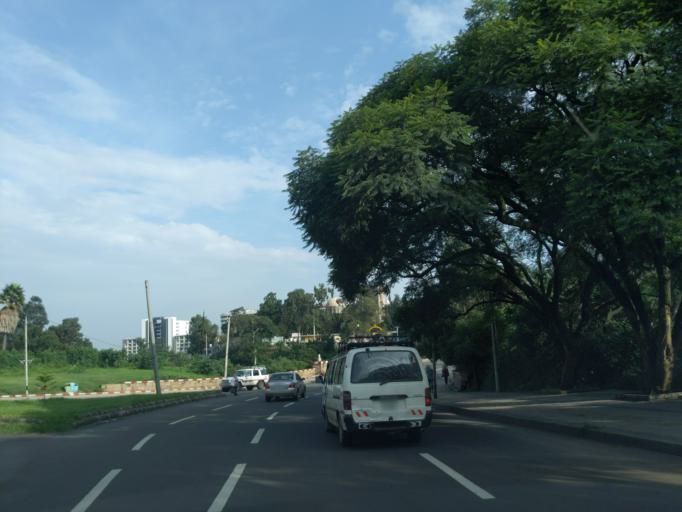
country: ET
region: Adis Abeba
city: Addis Ababa
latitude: 9.0143
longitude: 38.7628
